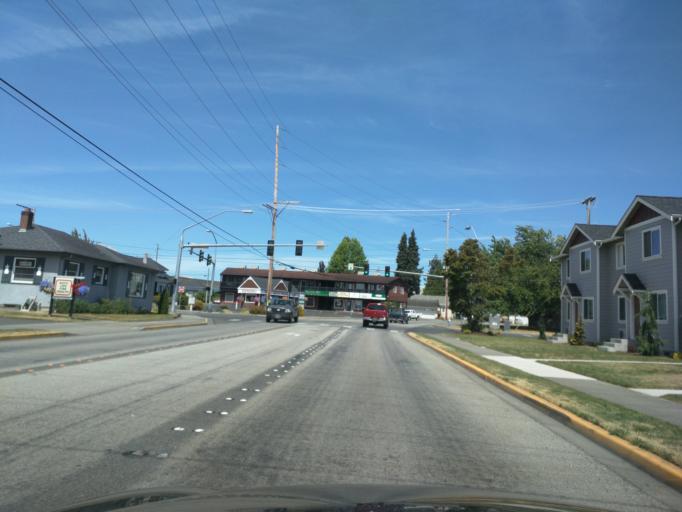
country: US
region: Washington
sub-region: Whatcom County
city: Lynden
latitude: 48.9447
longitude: -122.4484
